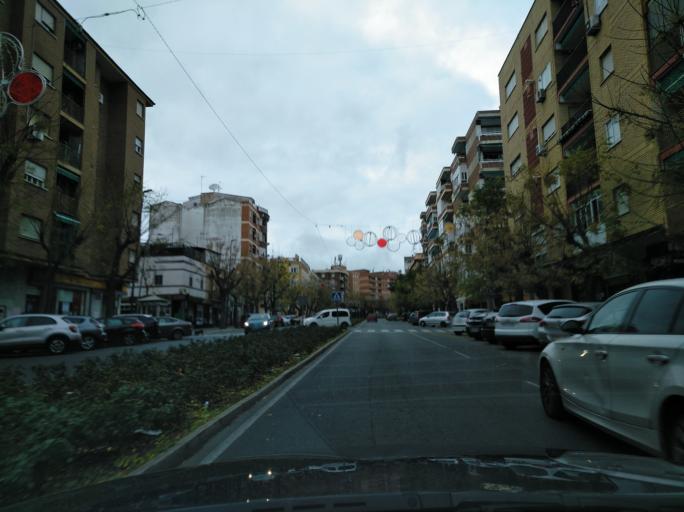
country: ES
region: Extremadura
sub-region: Provincia de Badajoz
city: Badajoz
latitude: 38.8870
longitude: -6.9813
